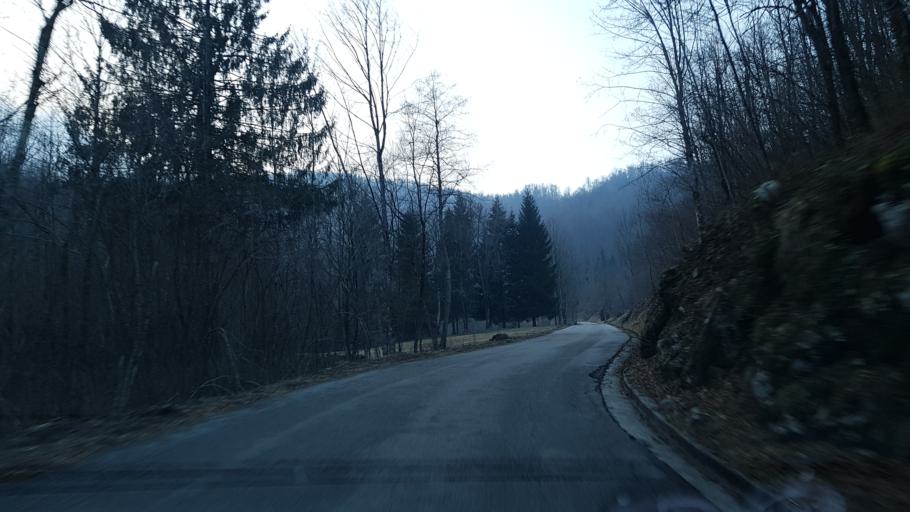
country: IT
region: Friuli Venezia Giulia
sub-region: Provincia di Udine
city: Taipana
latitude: 46.2164
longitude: 13.3903
